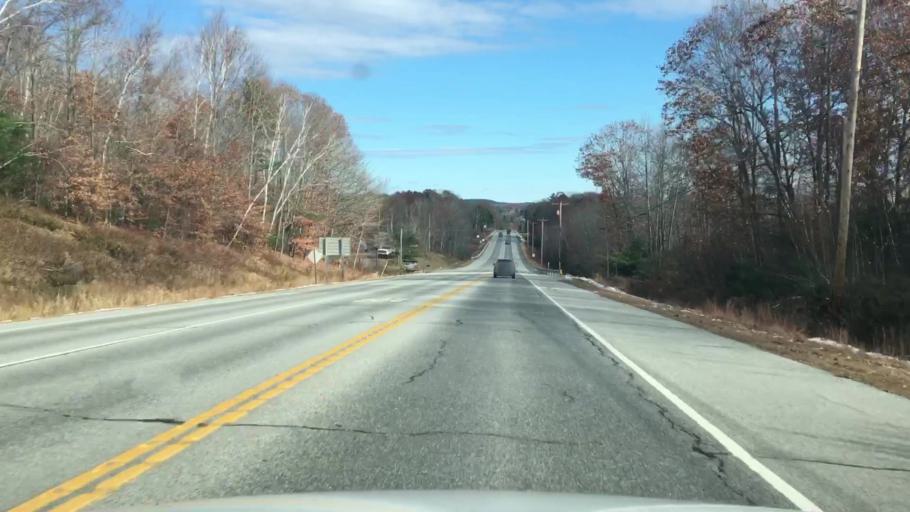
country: US
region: Maine
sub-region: Kennebec County
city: Winthrop
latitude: 44.3106
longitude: -69.9498
